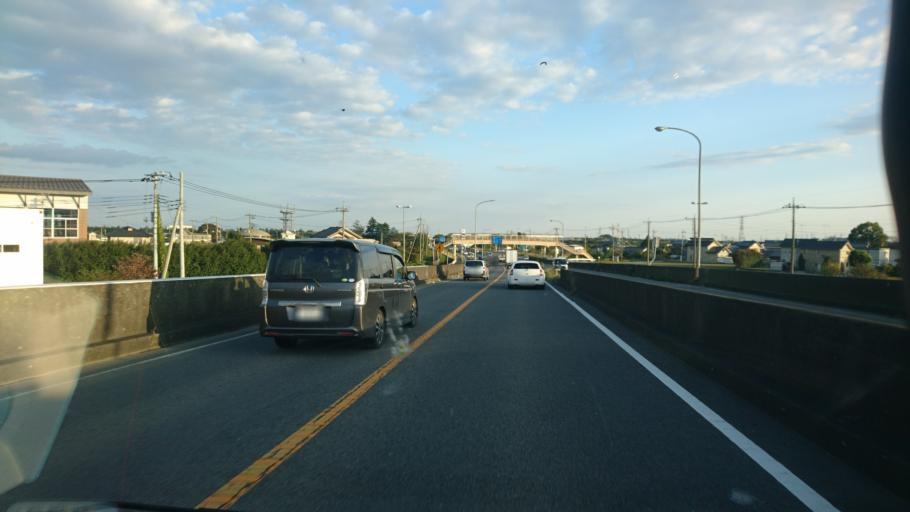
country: JP
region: Gunma
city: Ota
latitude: 36.3372
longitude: 139.3889
